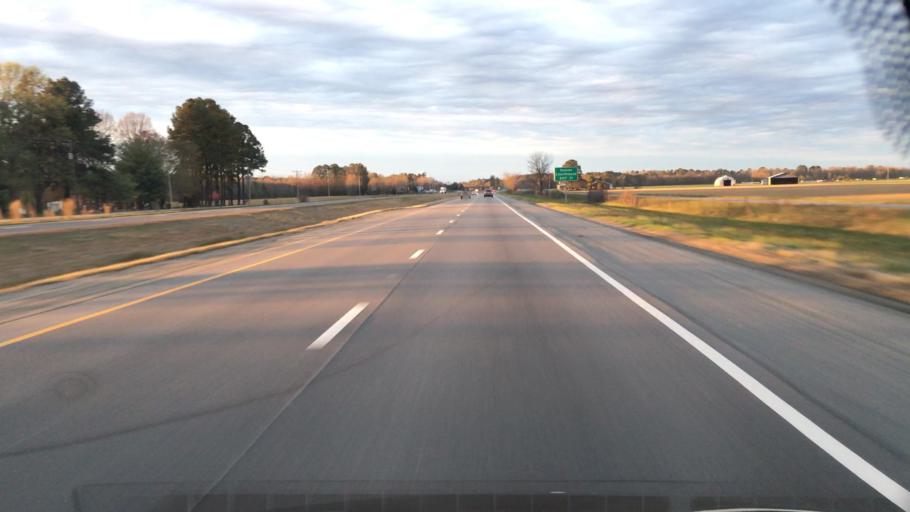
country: US
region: Virginia
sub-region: Sussex County
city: Sussex
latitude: 36.9300
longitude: -77.3947
